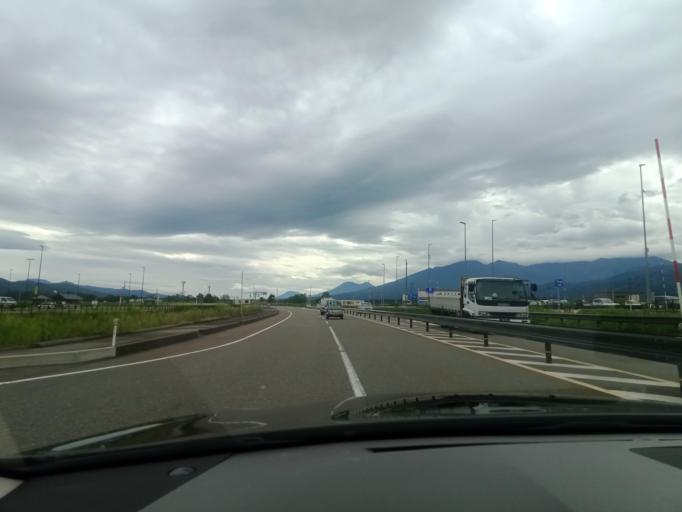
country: JP
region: Niigata
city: Arai
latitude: 37.0268
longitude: 138.2278
